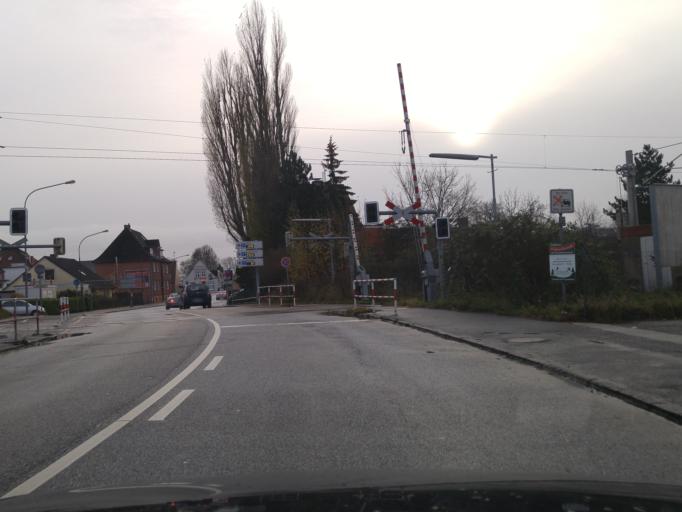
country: DE
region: Schleswig-Holstein
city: Travemuende
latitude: 53.9586
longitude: 10.8613
